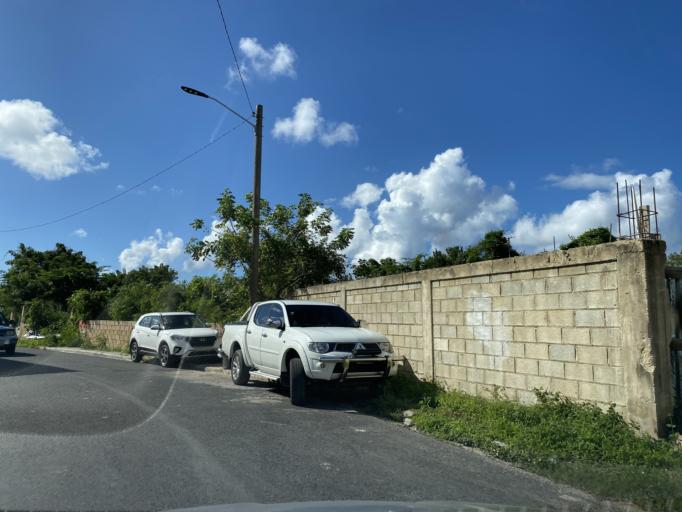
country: DO
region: La Romana
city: La Romana
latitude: 18.3692
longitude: -68.8372
